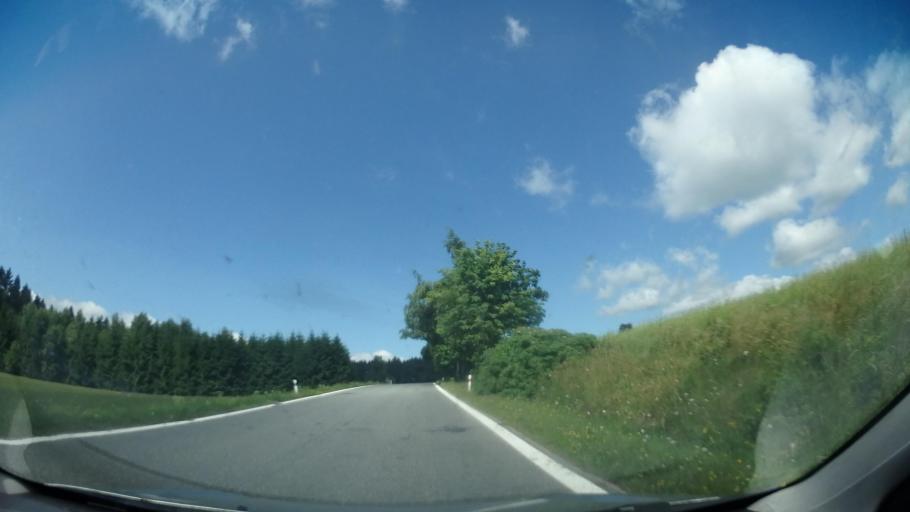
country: CZ
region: Vysocina
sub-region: Okres Zd'ar nad Sazavou
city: Nove Mesto na Morave
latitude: 49.6162
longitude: 16.0290
